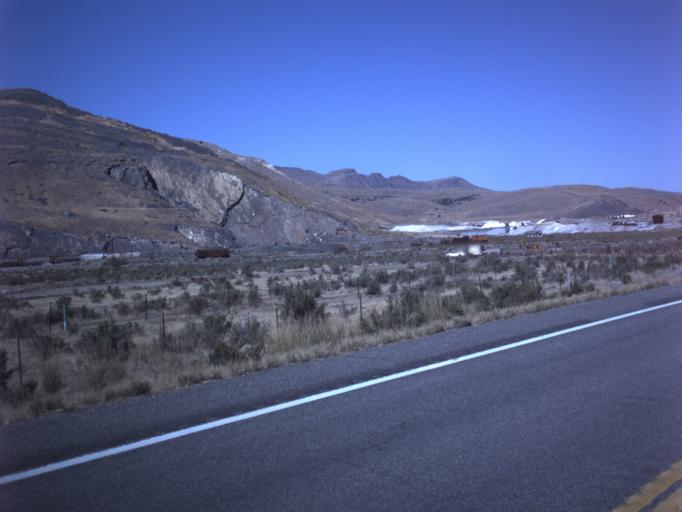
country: US
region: Utah
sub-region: Tooele County
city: Grantsville
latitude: 40.6745
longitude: -112.5497
